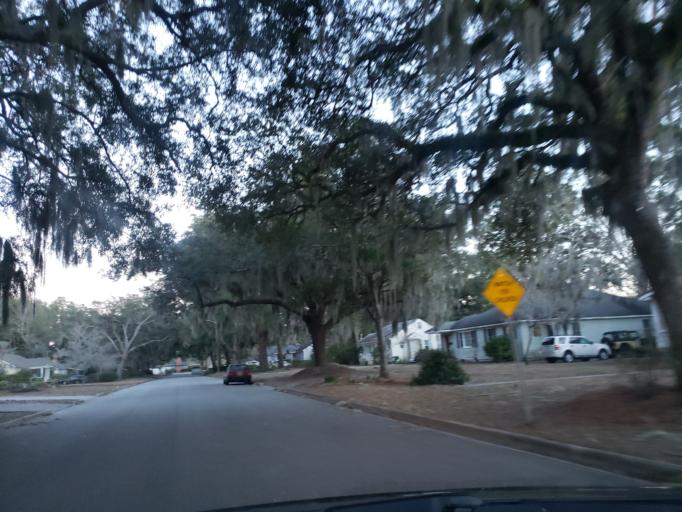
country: US
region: Georgia
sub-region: Chatham County
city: Thunderbolt
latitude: 32.0199
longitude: -81.0810
